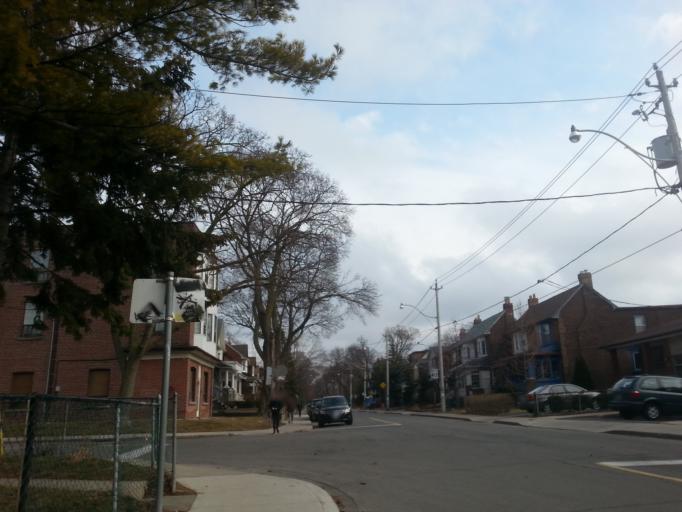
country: CA
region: Ontario
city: Toronto
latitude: 43.6773
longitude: -79.4289
